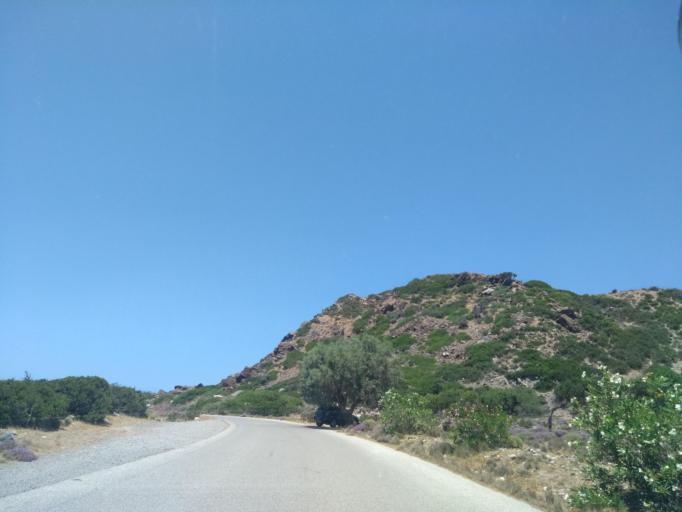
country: GR
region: Crete
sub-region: Nomos Chanias
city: Vryses
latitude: 35.3495
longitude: 23.5386
